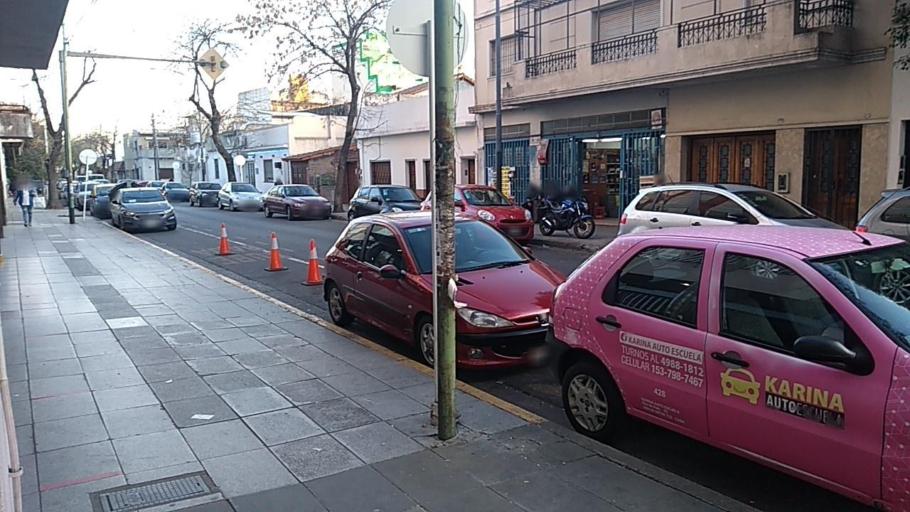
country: AR
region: Buenos Aires F.D.
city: Villa Santa Rita
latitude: -34.6195
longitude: -58.5046
